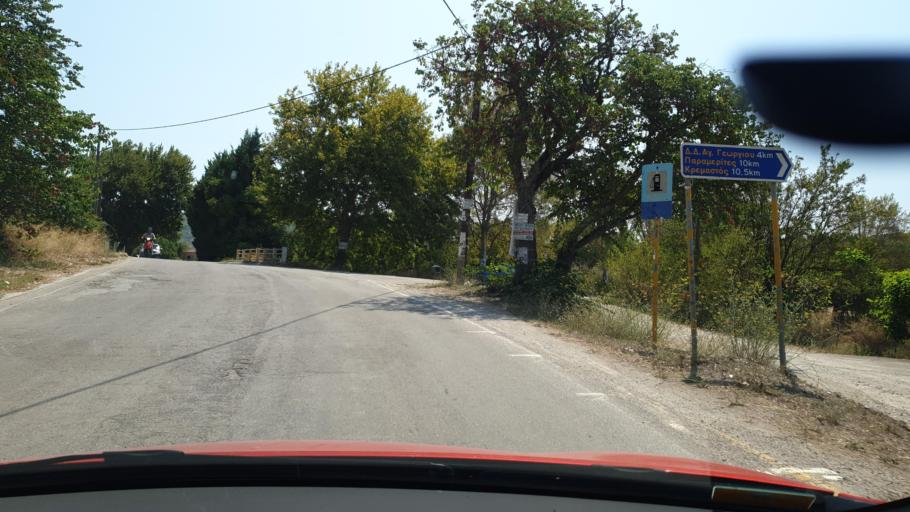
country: GR
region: Central Greece
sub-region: Nomos Evvoias
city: Oxilithos
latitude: 38.4979
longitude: 24.1107
